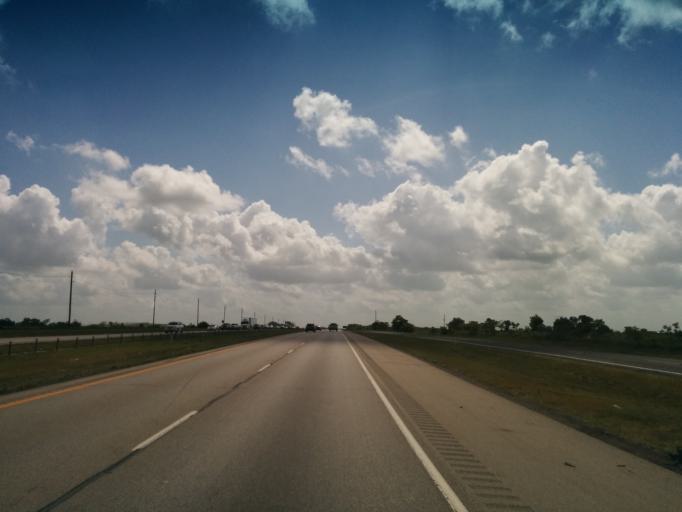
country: US
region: Texas
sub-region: Austin County
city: Sealy
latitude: 29.7563
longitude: -96.2367
